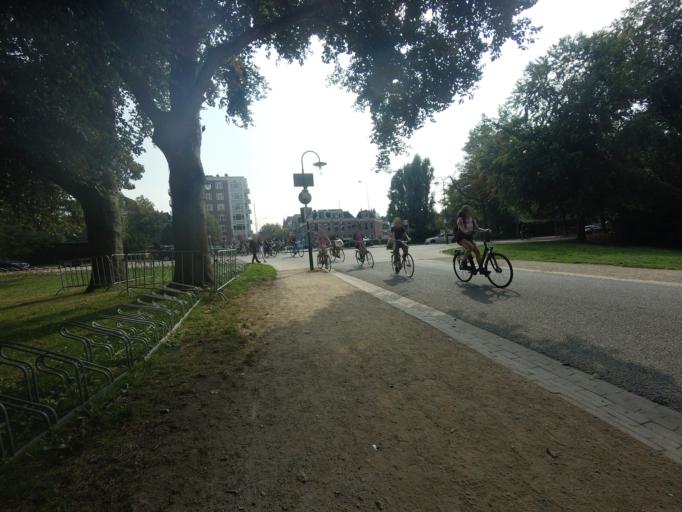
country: NL
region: Groningen
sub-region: Gemeente Groningen
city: Groningen
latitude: 53.2197
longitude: 6.5558
